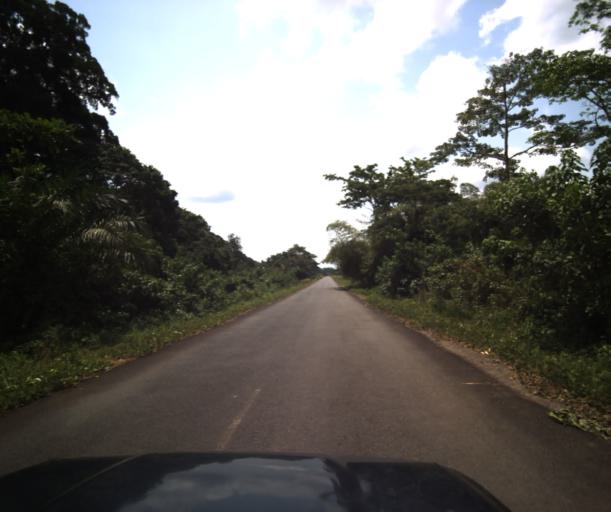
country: CM
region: Centre
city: Eseka
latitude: 3.8198
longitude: 10.8045
